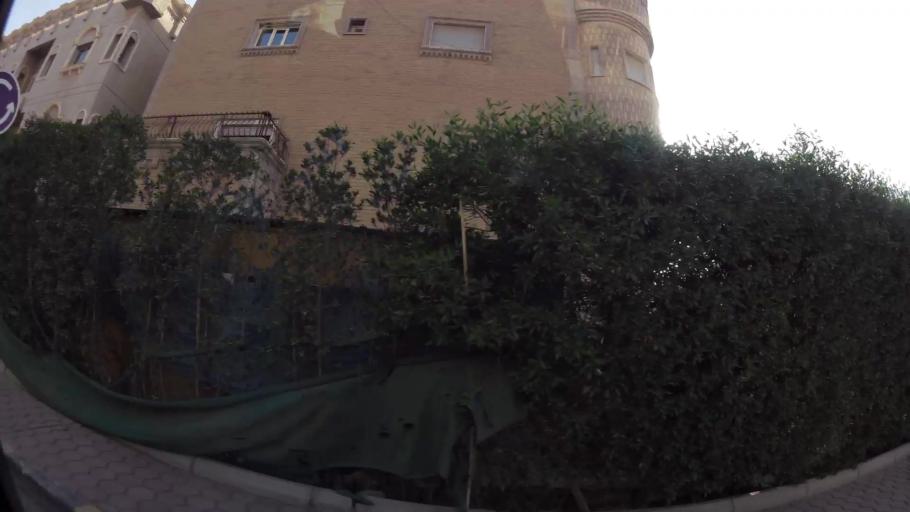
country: KW
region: Al Asimah
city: Ar Rabiyah
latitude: 29.3008
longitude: 47.7970
